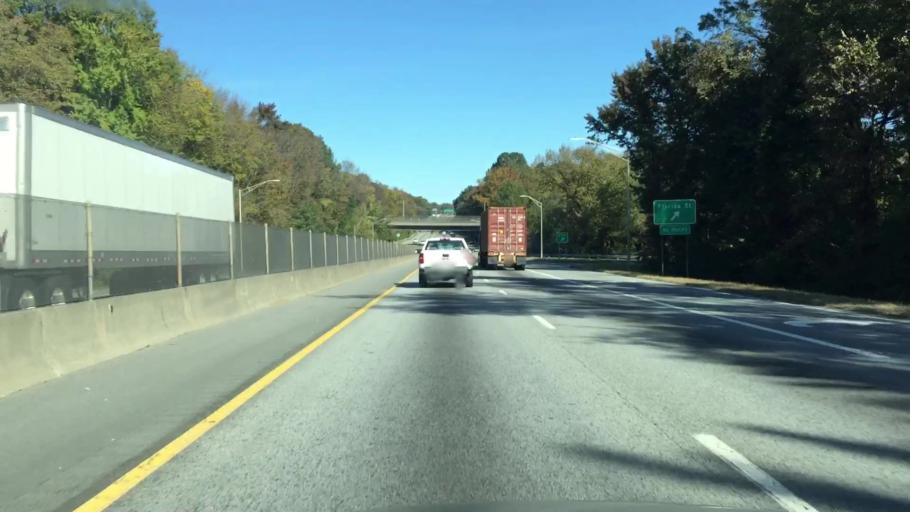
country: US
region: North Carolina
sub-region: Guilford County
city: Greensboro
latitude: 36.0517
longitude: -79.7681
